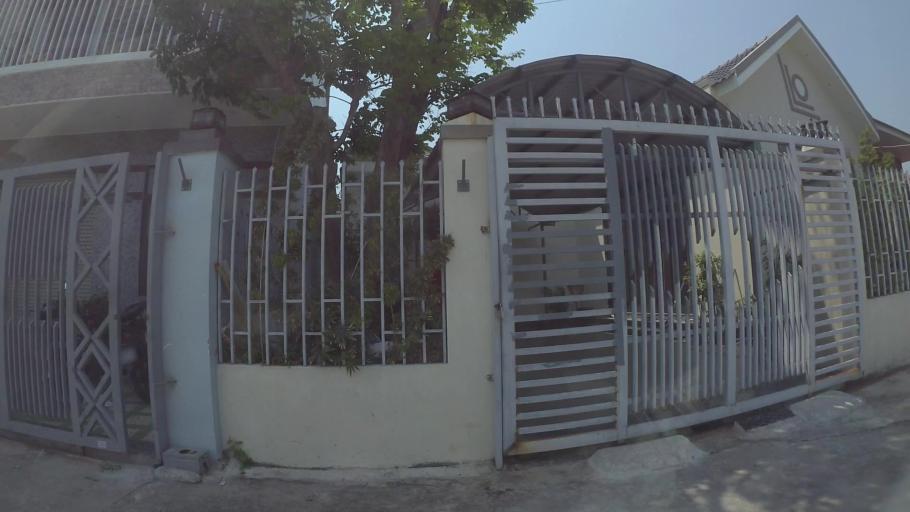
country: VN
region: Da Nang
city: Ngu Hanh Son
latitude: 15.9967
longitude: 108.2652
